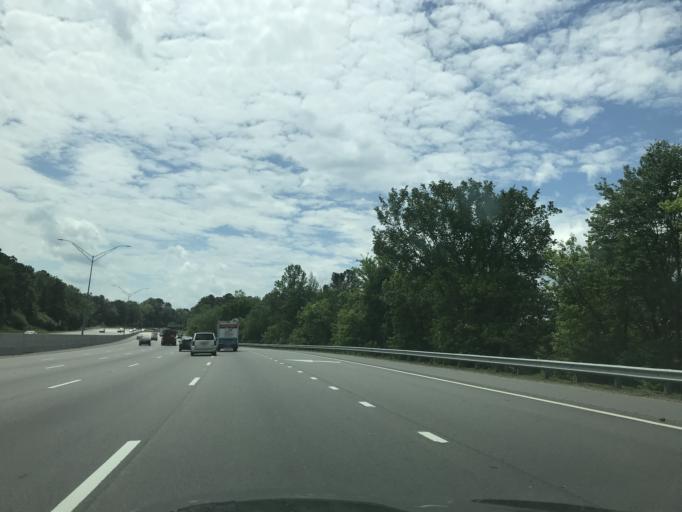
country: US
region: North Carolina
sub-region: Wake County
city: Raleigh
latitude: 35.7566
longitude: -78.6186
